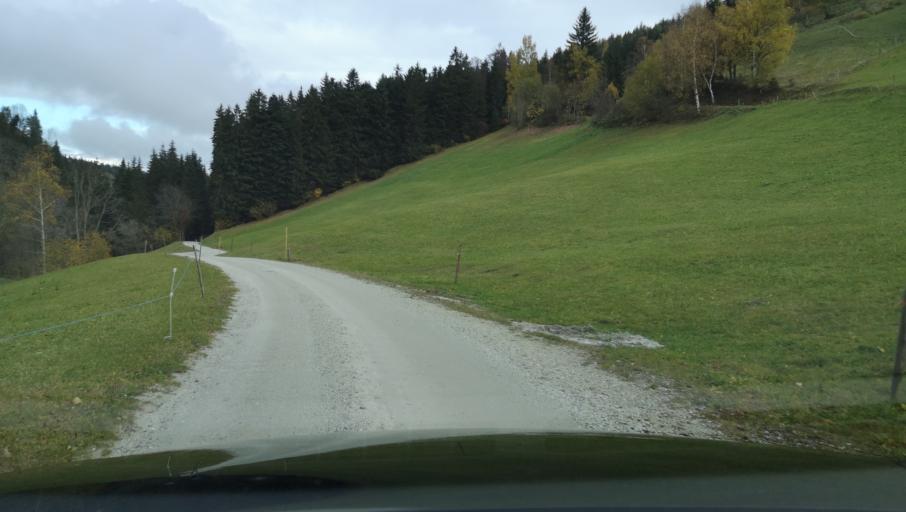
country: AT
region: Styria
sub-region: Politischer Bezirk Weiz
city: Gasen
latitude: 47.3751
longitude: 15.6090
